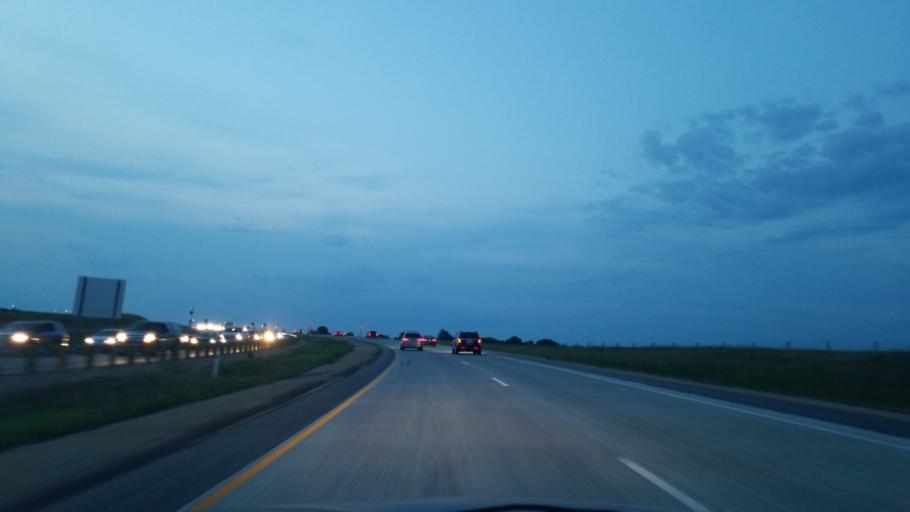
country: US
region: Minnesota
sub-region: Washington County
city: Oak Park Heights
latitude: 45.0495
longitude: -92.7789
